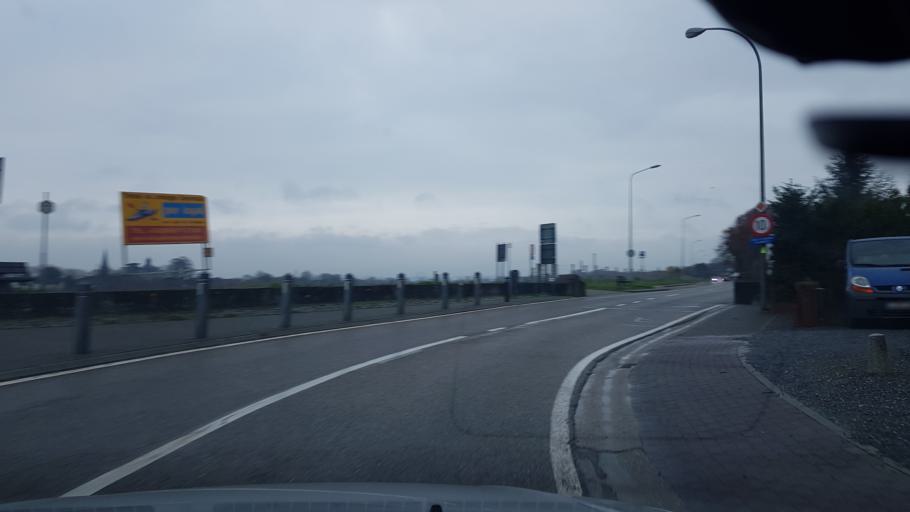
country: BE
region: Flanders
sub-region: Provincie Limburg
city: Lanaken
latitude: 50.8808
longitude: 5.6781
